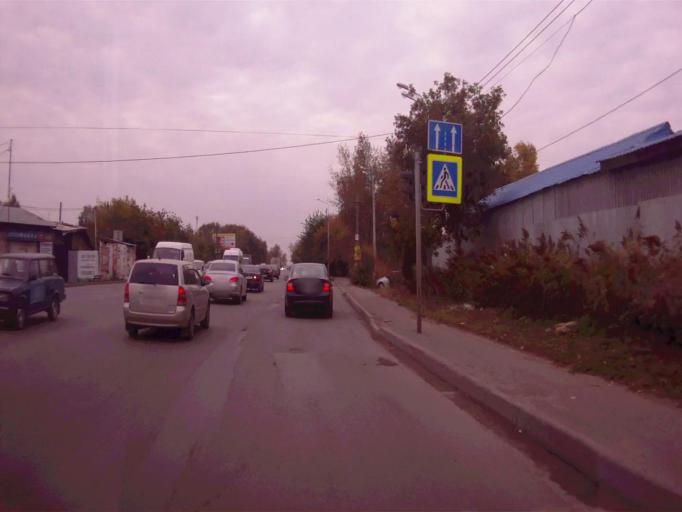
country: RU
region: Chelyabinsk
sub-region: Gorod Chelyabinsk
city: Chelyabinsk
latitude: 55.1312
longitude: 61.3852
